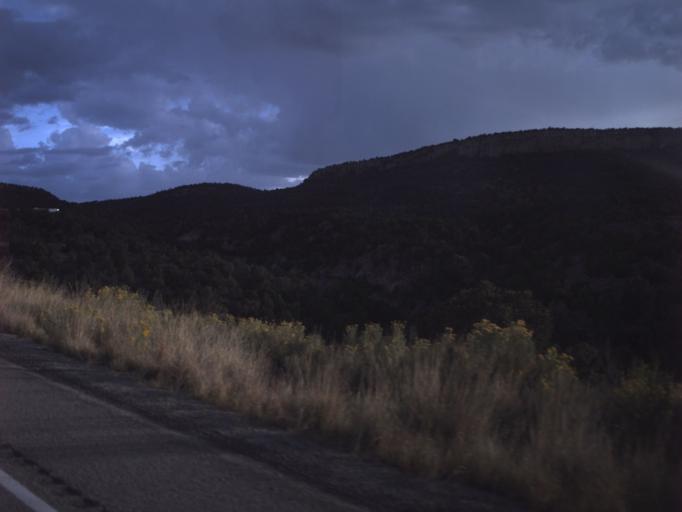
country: US
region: Utah
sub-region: San Juan County
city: Monticello
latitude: 38.0034
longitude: -109.3535
